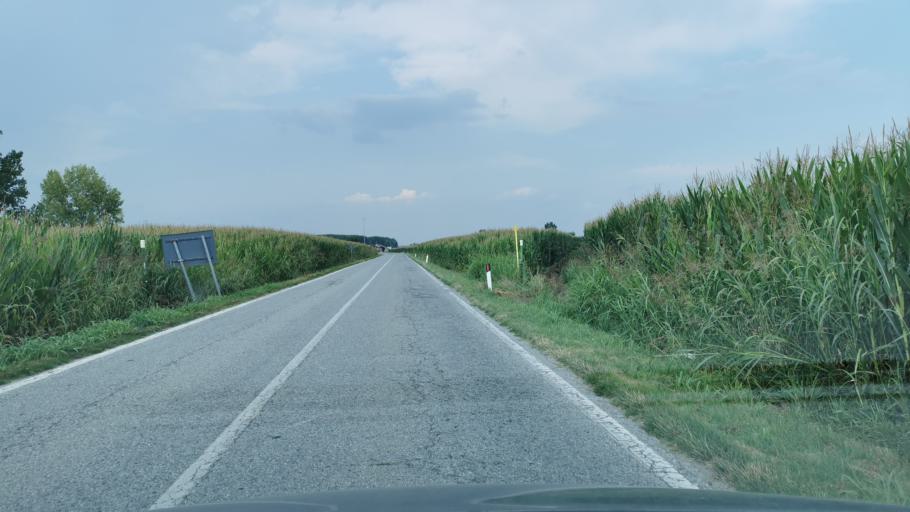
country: IT
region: Piedmont
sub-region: Provincia di Cuneo
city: Vottignasco
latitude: 44.5672
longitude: 7.5883
